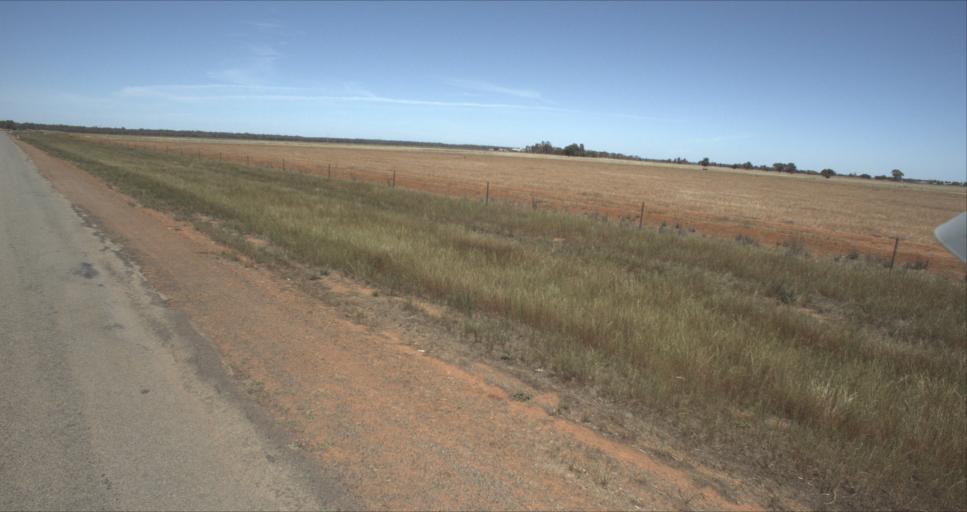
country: AU
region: New South Wales
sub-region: Leeton
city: Leeton
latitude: -34.5787
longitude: 146.3092
